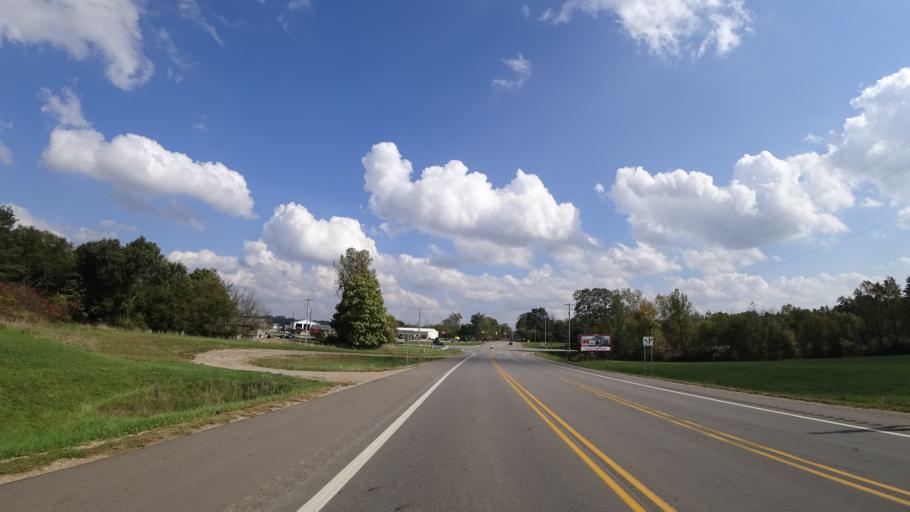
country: US
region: Michigan
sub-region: Calhoun County
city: Athens
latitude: 42.0614
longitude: -85.2364
